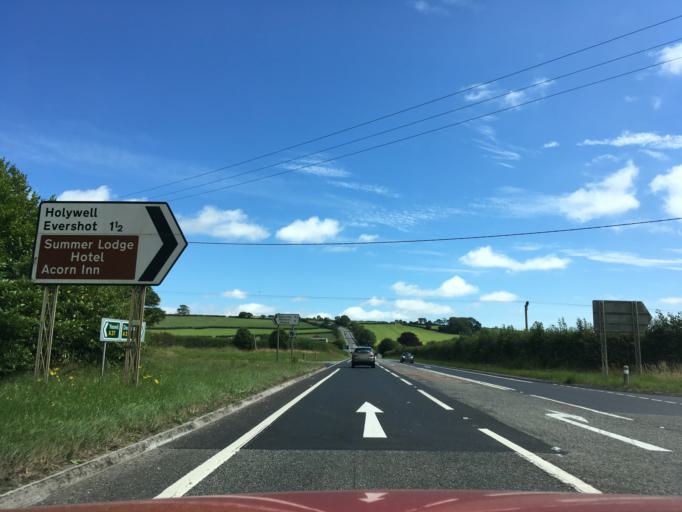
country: GB
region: England
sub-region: Somerset
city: Yeovil
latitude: 50.8370
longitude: -2.5775
